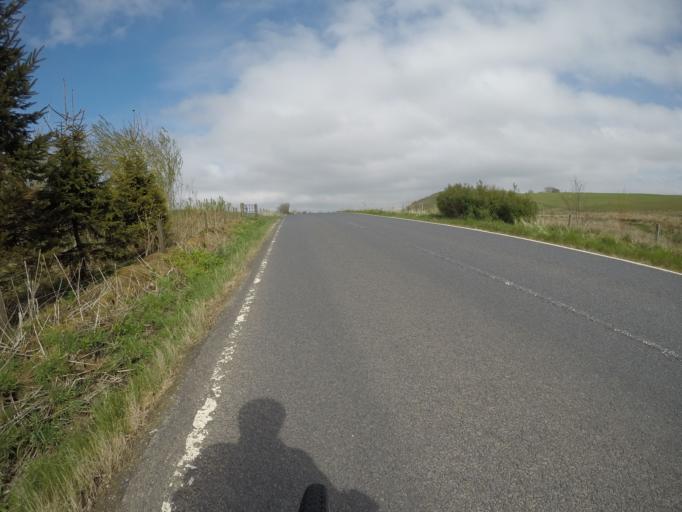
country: GB
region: Scotland
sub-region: East Renfrewshire
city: Neilston
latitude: 55.7265
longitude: -4.4229
